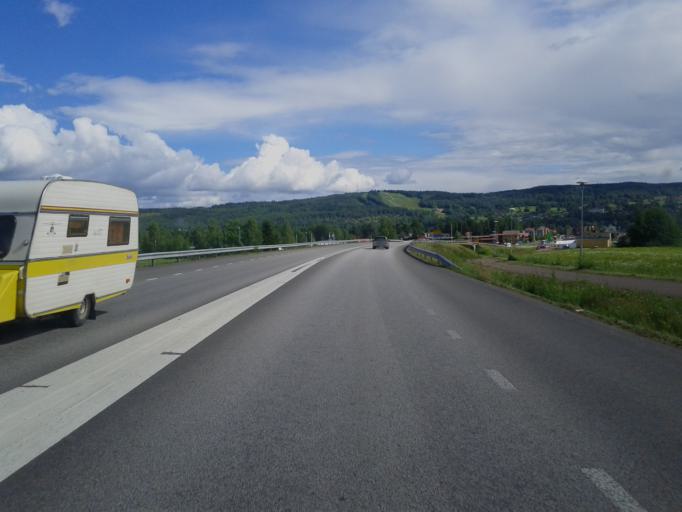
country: SE
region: Dalarna
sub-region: Rattviks Kommun
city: Raettvik
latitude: 60.8929
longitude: 15.1052
